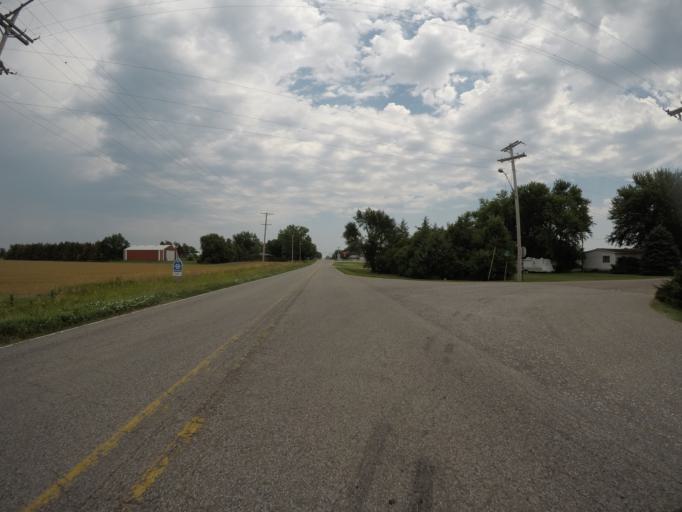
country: US
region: Nebraska
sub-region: Adams County
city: Hastings
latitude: 40.5971
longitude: -98.5093
